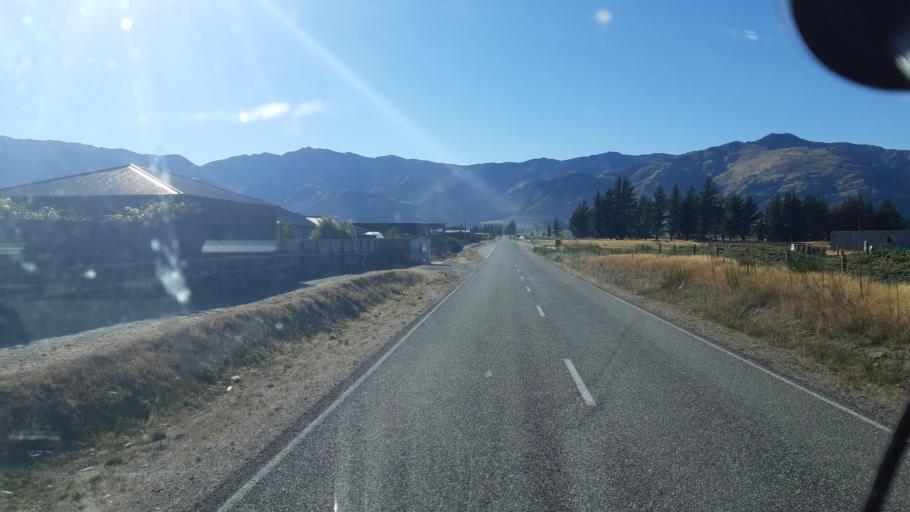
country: NZ
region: Otago
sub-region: Queenstown-Lakes District
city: Wanaka
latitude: -44.6185
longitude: 169.2551
